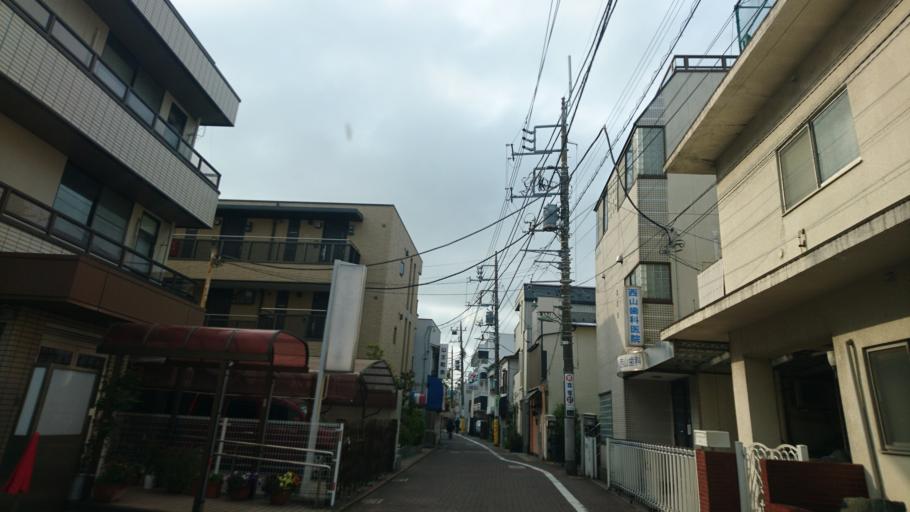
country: JP
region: Kanagawa
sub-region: Kawasaki-shi
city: Kawasaki
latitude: 35.5939
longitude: 139.7250
